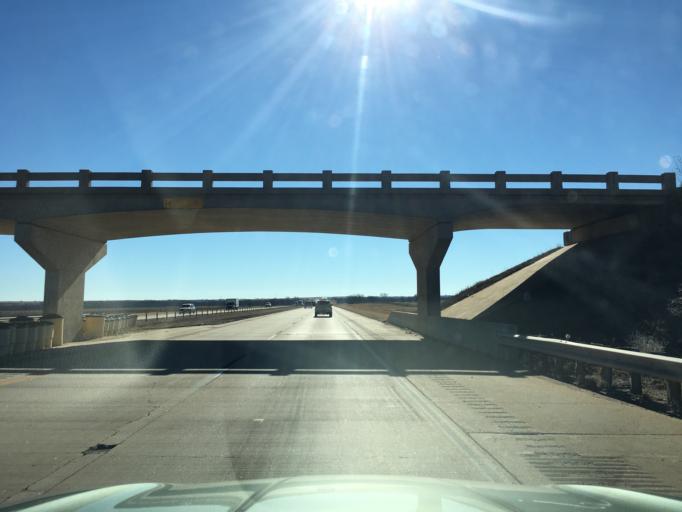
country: US
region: Oklahoma
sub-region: Noble County
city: Perry
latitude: 36.4495
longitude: -97.3271
